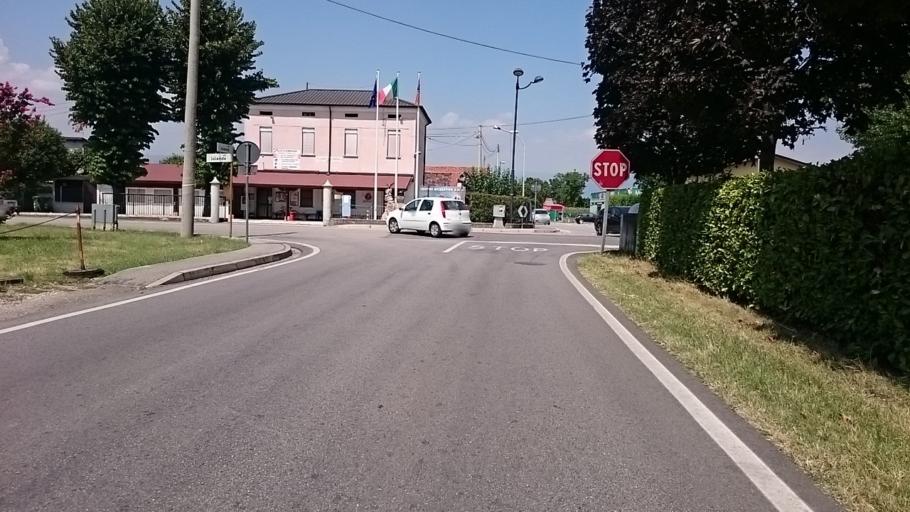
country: IT
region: Veneto
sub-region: Provincia di Vicenza
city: Rosa
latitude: 45.6831
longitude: 11.7400
